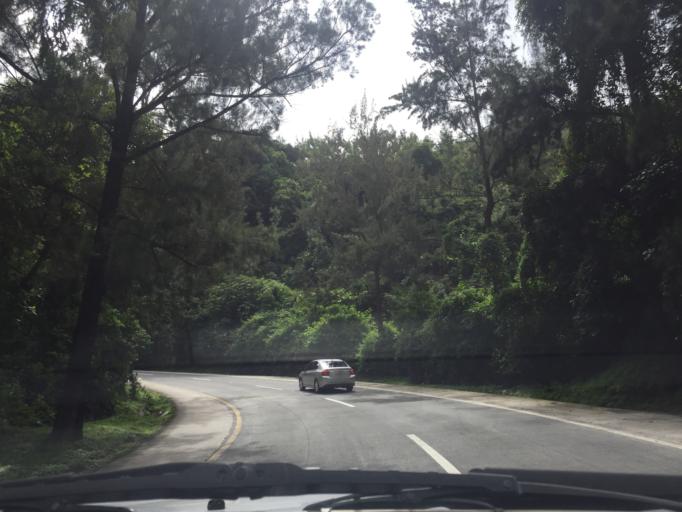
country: GT
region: Sacatepequez
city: Antigua Guatemala
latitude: 14.5581
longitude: -90.7046
